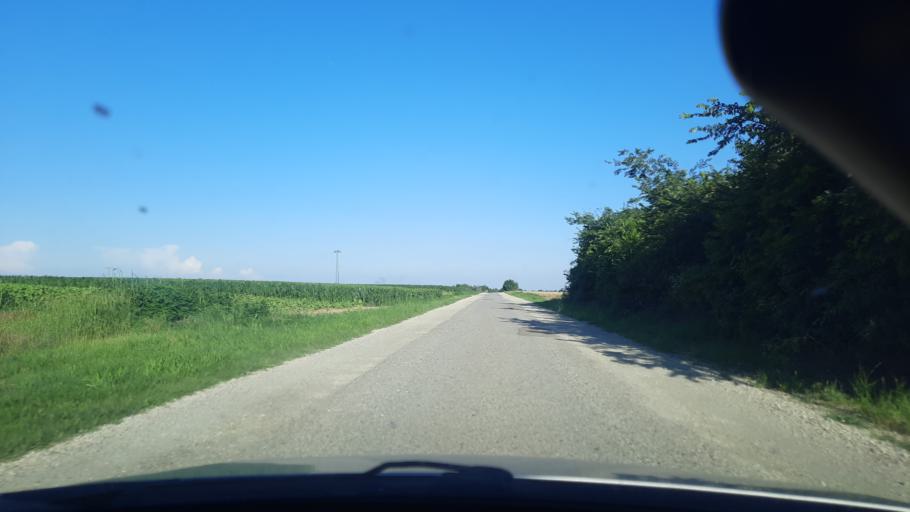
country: RS
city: Cortanovci
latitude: 45.1113
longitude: 19.9707
